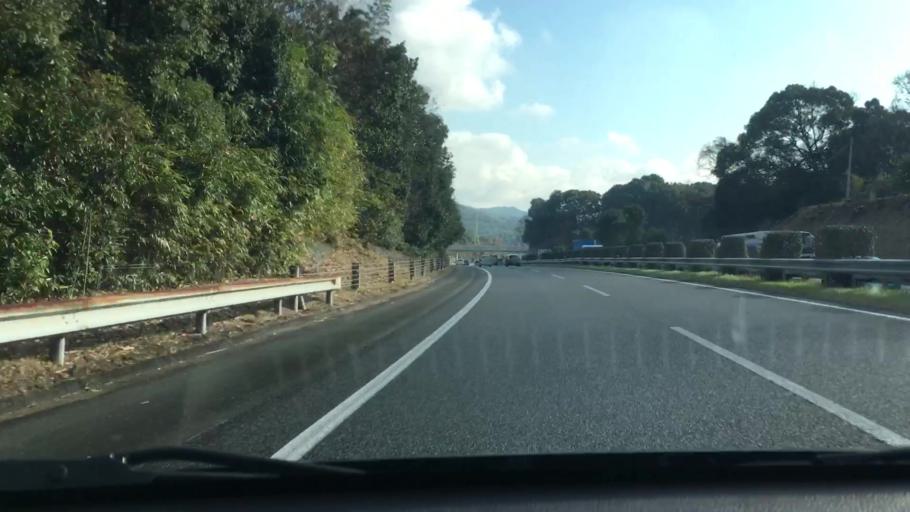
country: JP
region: Kumamoto
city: Matsubase
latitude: 32.6402
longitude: 130.7075
